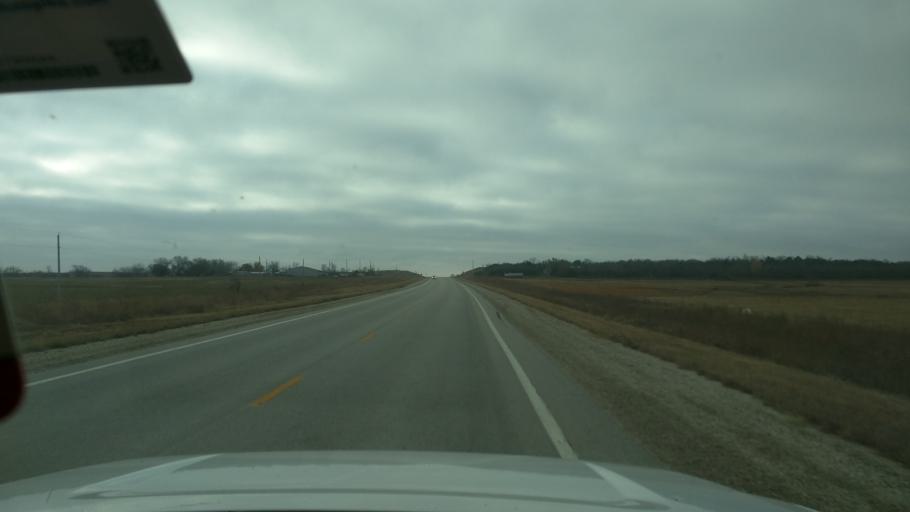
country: US
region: Kansas
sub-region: Elk County
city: Howard
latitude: 37.6109
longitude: -96.2535
